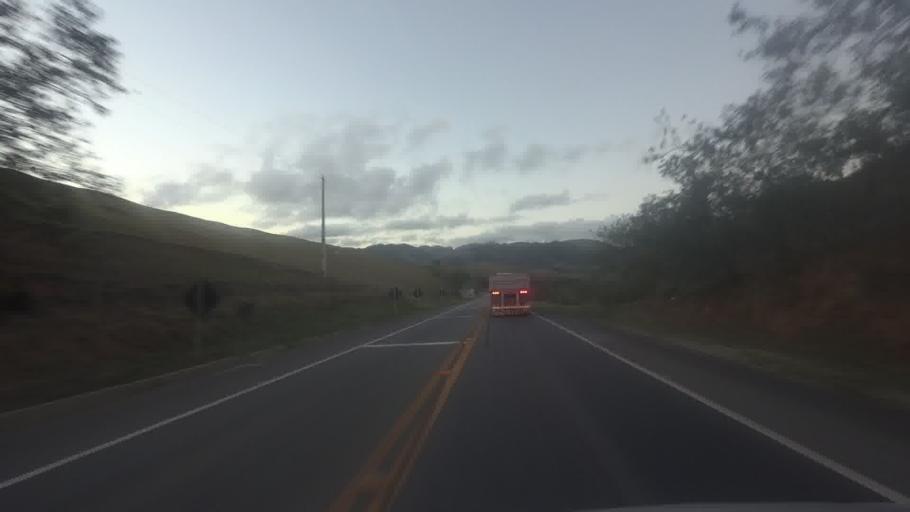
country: BR
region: Espirito Santo
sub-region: Rio Novo Do Sul
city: Rio Novo do Sul
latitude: -20.8598
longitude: -40.8760
